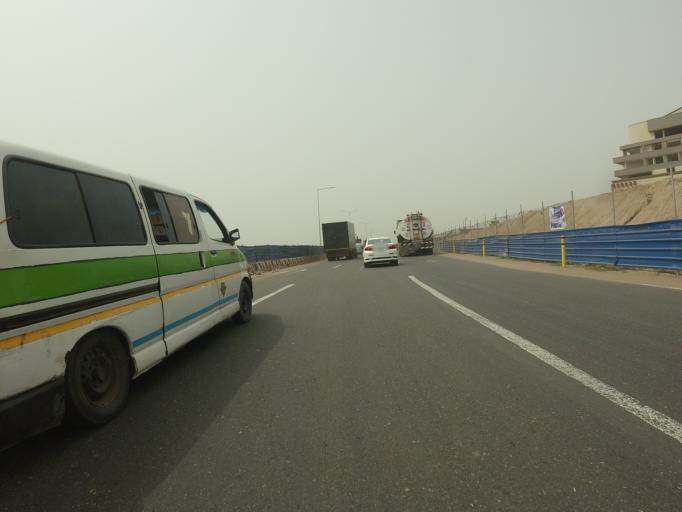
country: GH
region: Greater Accra
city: Tema
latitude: 5.6861
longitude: -0.0157
